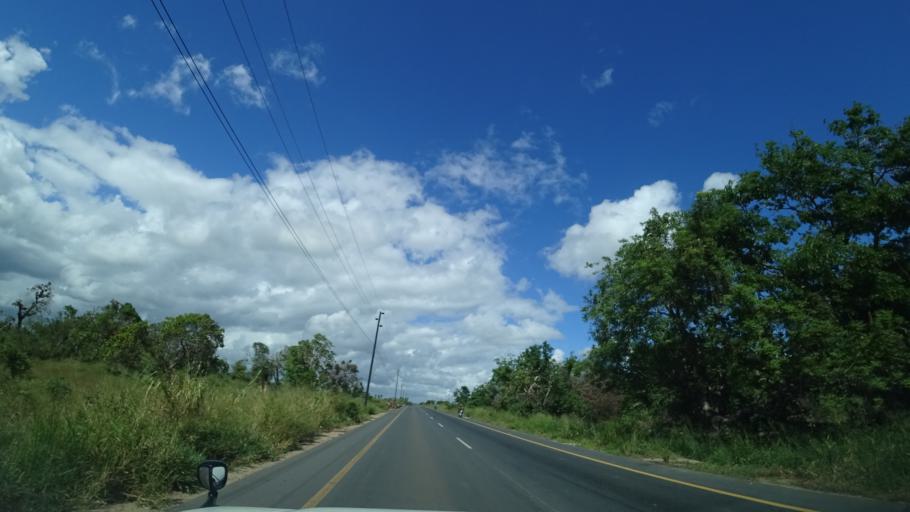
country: MZ
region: Sofala
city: Dondo
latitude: -19.5032
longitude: 34.6015
